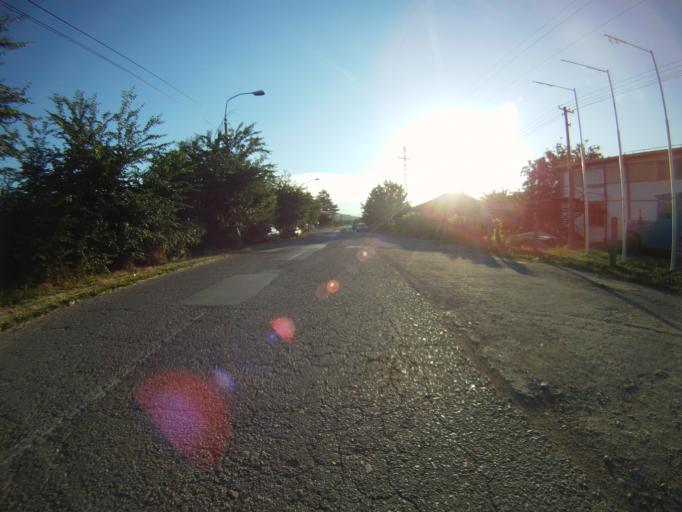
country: RS
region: Central Serbia
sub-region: Nisavski Okrug
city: Niska Banja
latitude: 43.2999
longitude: 22.0015
